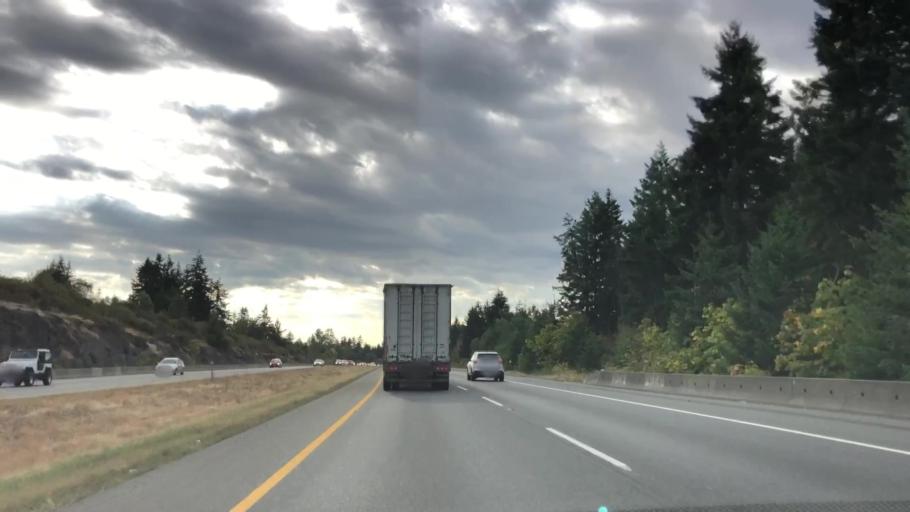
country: CA
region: British Columbia
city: Nanaimo
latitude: 49.1949
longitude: -124.0215
